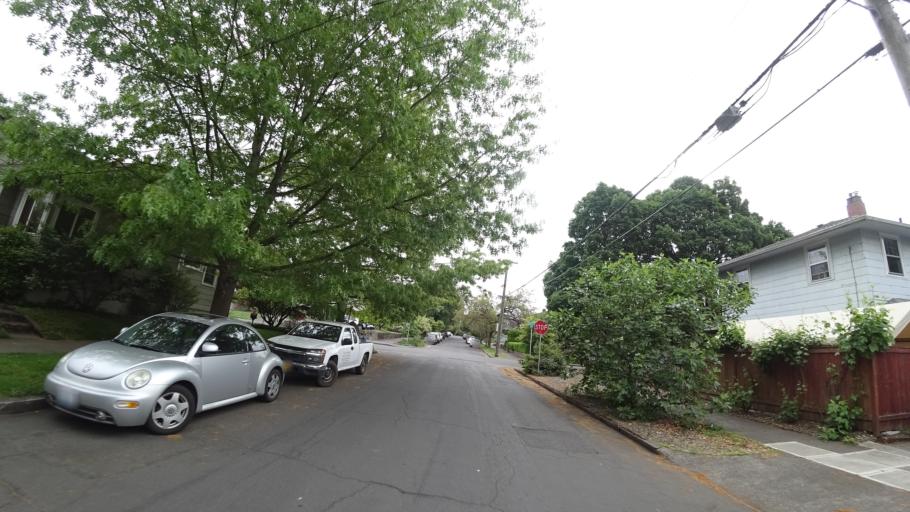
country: US
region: Oregon
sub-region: Multnomah County
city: Portland
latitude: 45.5005
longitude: -122.6360
